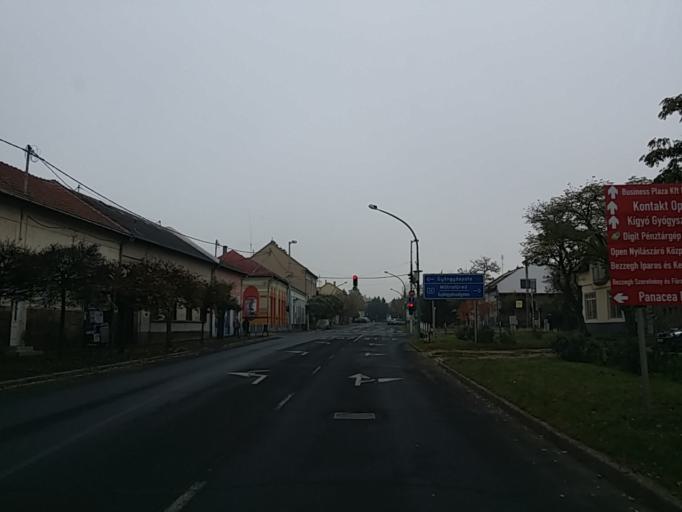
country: HU
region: Heves
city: Gyongyos
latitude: 47.7800
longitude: 19.9230
